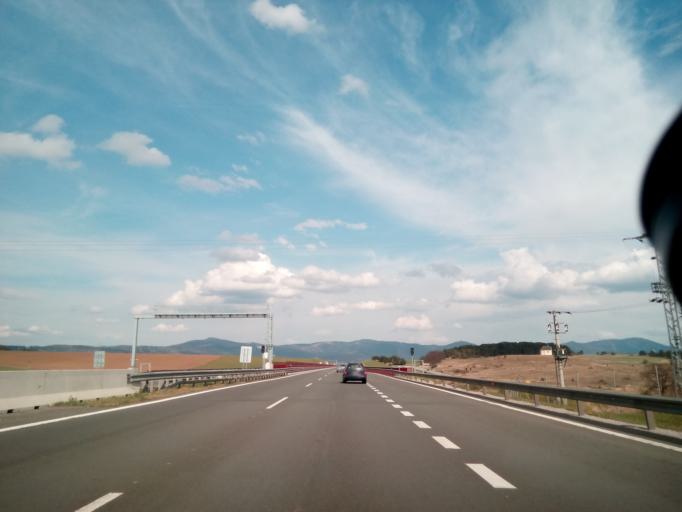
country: SK
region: Presovsky
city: Spisske Podhradie
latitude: 49.0077
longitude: 20.7110
